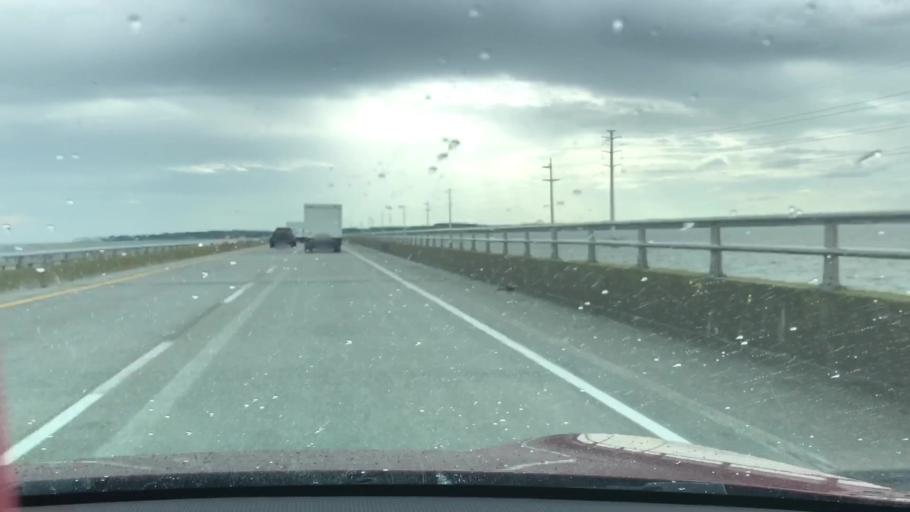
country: US
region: North Carolina
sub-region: Dare County
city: Southern Shores
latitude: 36.0867
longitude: -75.7642
